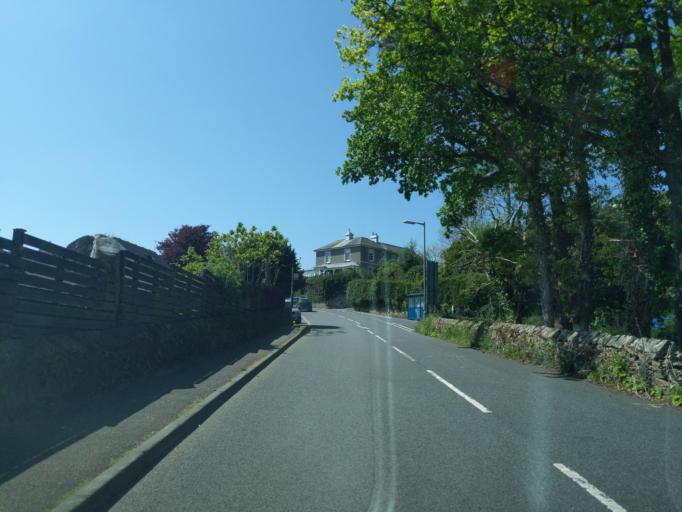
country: GB
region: England
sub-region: Cornwall
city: Pillaton
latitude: 50.3939
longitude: -4.3094
